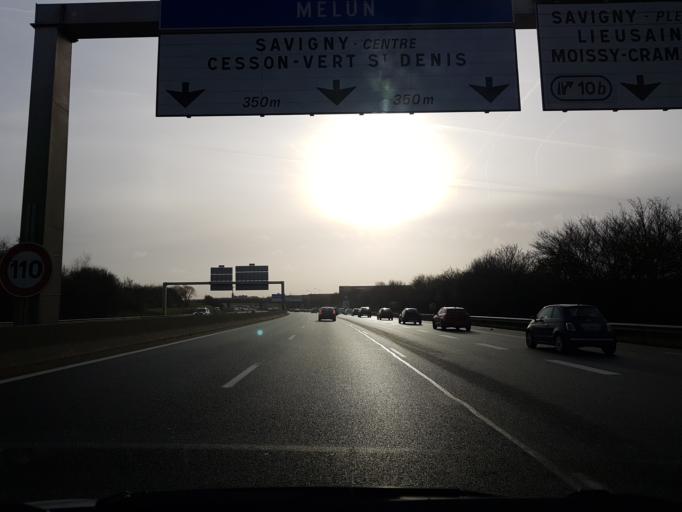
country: FR
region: Ile-de-France
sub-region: Departement de Seine-et-Marne
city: Lieusaint
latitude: 48.6260
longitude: 2.5393
